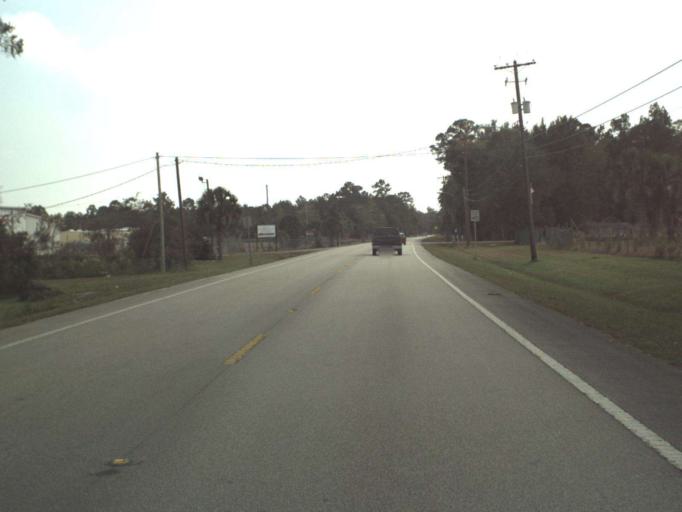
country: US
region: Florida
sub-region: Leon County
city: Woodville
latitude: 30.1716
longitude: -84.2092
